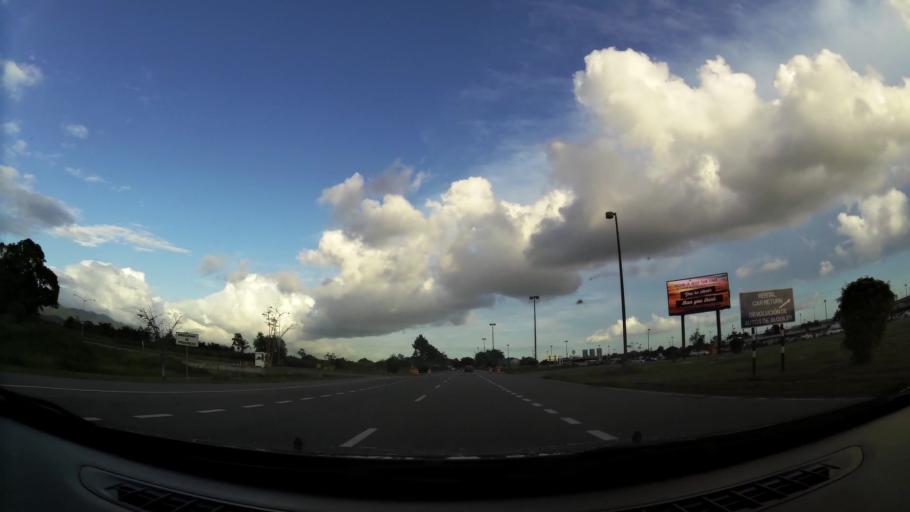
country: TT
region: Tunapuna/Piarco
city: Arouca
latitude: 10.6044
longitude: -61.3414
